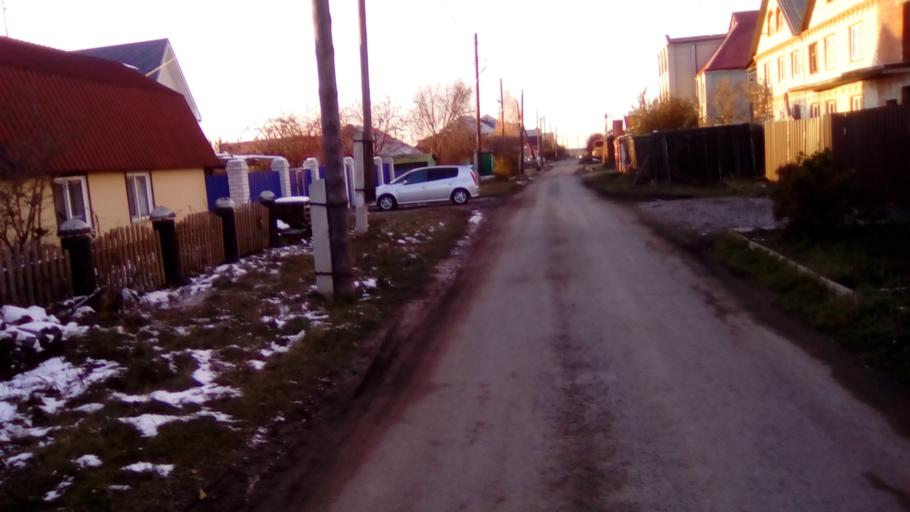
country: RU
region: Tjumen
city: Moskovskiy
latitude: 57.2208
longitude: 65.3653
